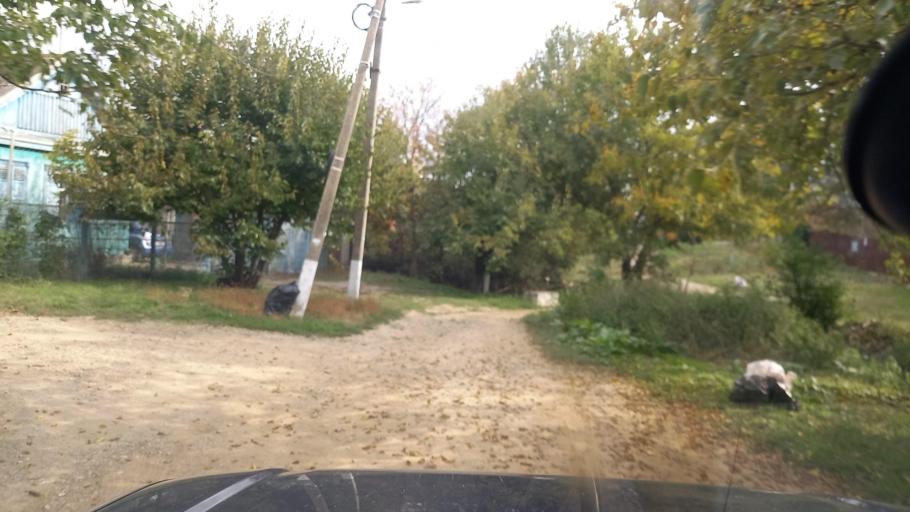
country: RU
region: Krasnodarskiy
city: Il'skiy
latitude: 44.8487
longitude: 38.5634
